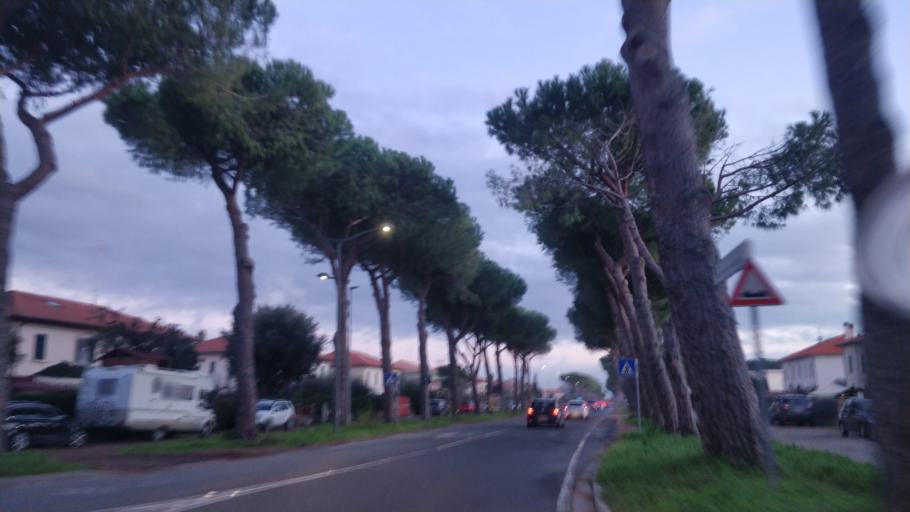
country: IT
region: Tuscany
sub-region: Provincia di Livorno
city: Rosignano Solvay-Castiglioncello
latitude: 43.3863
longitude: 10.4359
